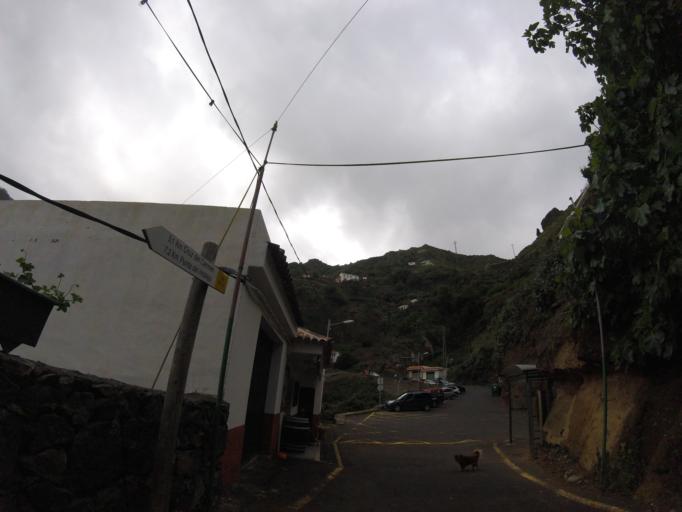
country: ES
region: Canary Islands
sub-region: Provincia de Santa Cruz de Tenerife
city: Tegueste
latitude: 28.5479
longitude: -16.2965
